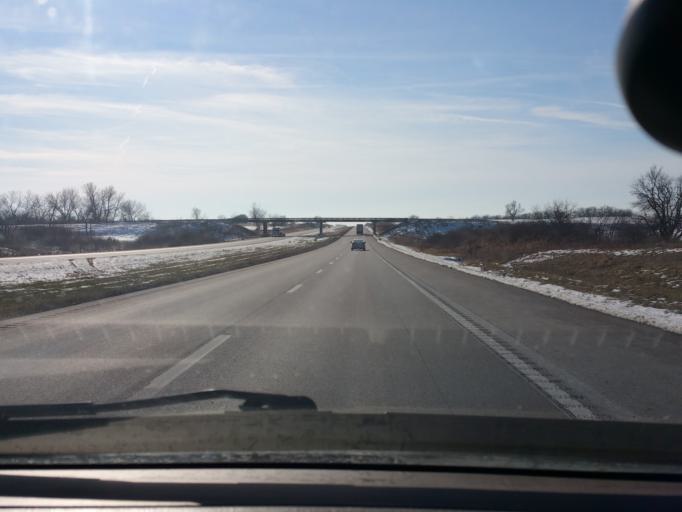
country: US
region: Missouri
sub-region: Clinton County
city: Cameron
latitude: 39.8058
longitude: -94.1981
